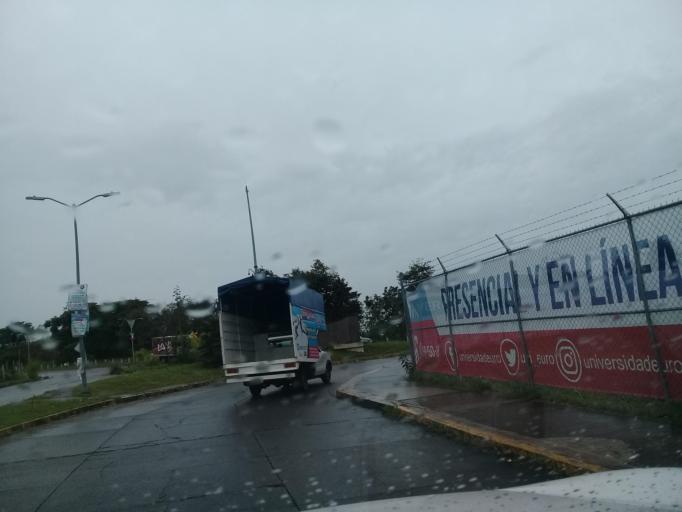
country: MX
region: Veracruz
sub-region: Emiliano Zapata
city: Las Trancas
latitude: 19.5047
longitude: -96.8573
